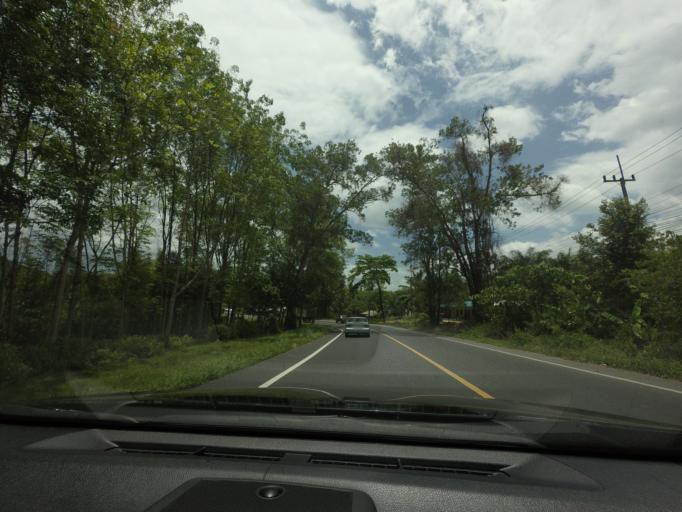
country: TH
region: Phangnga
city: Kapong
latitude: 8.5664
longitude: 98.4306
